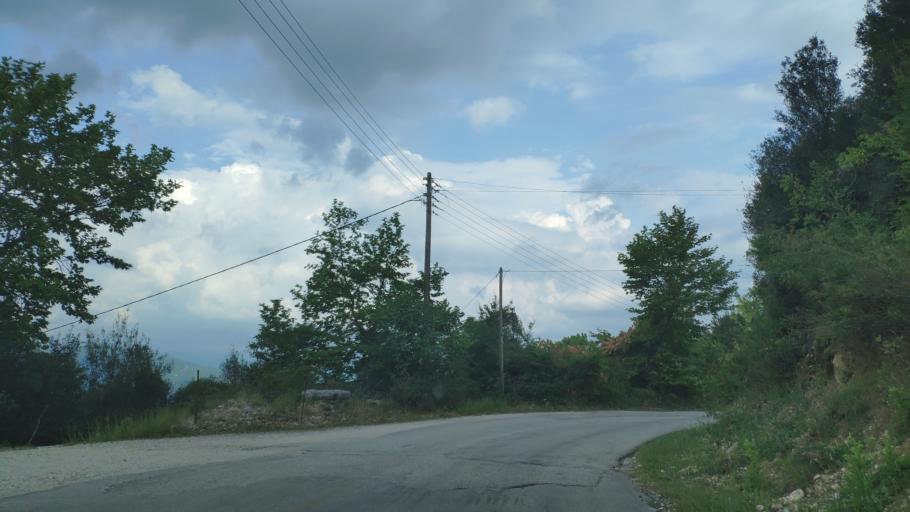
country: GR
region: Epirus
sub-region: Nomos Artas
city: Agios Dimitrios
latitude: 39.3817
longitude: 21.0252
